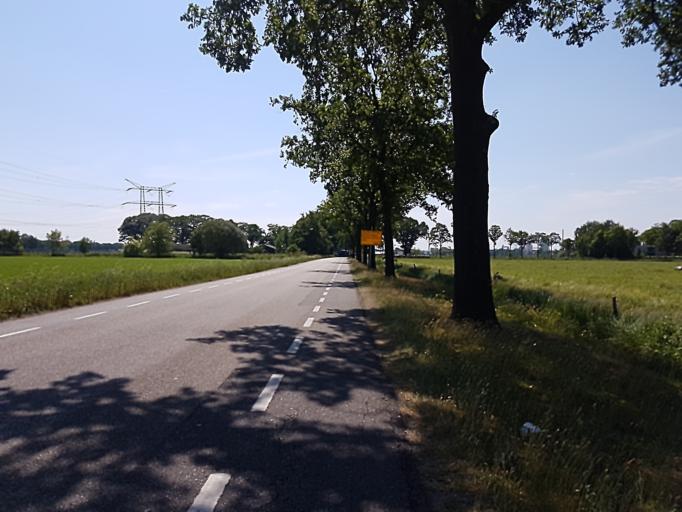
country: NL
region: North Brabant
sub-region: Gemeente Dongen
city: Dongen
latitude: 51.6257
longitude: 4.9978
